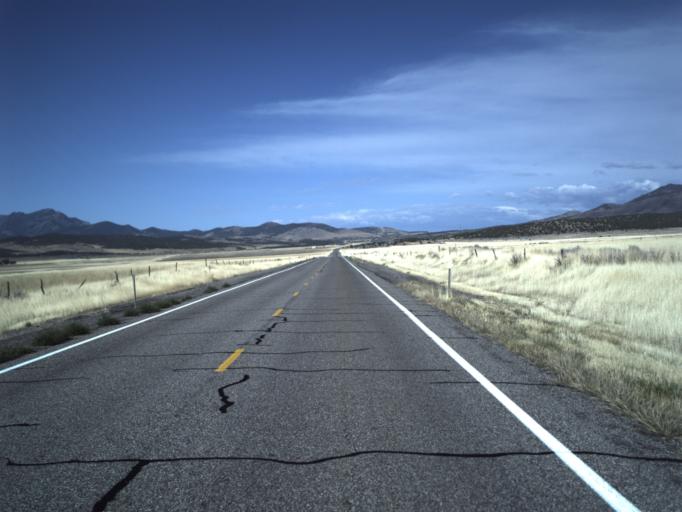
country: US
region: Utah
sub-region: Millard County
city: Fillmore
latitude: 39.1164
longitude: -112.2623
